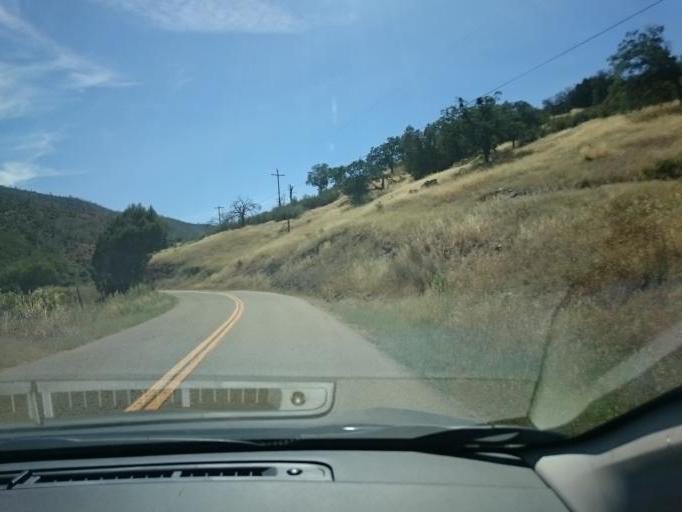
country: US
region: California
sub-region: Stanislaus County
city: Patterson
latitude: 37.4160
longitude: -121.3965
